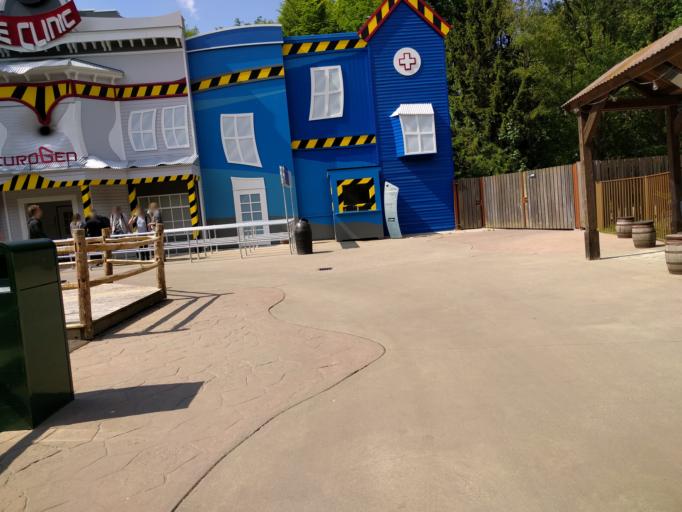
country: NL
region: Gelderland
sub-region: Gemeente Nunspeet
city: Nunspeet
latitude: 52.4429
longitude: 5.7671
